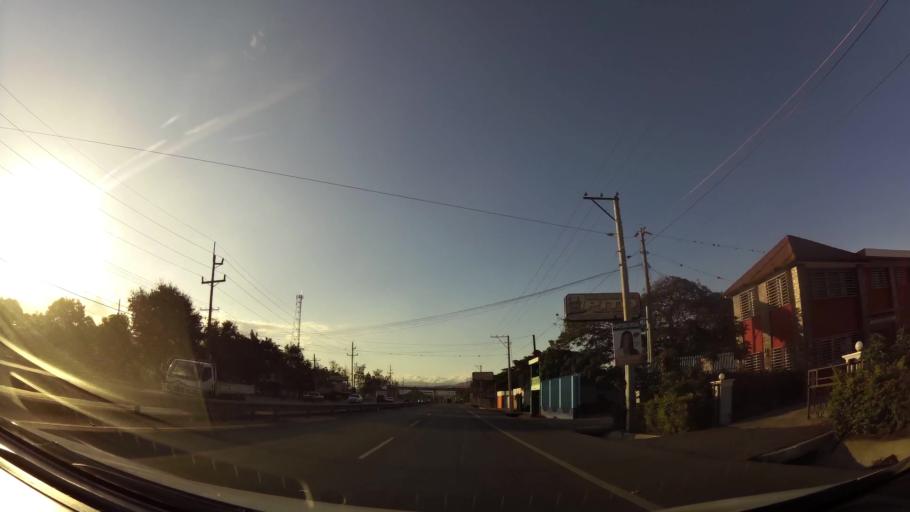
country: DO
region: Santiago
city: Palmar Arriba
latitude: 19.5103
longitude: -70.7571
